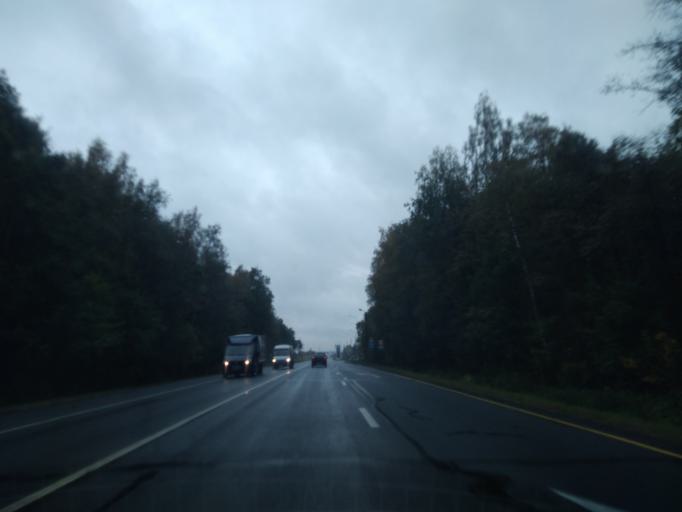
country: RU
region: Tula
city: Barsuki
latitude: 54.2694
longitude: 37.5341
